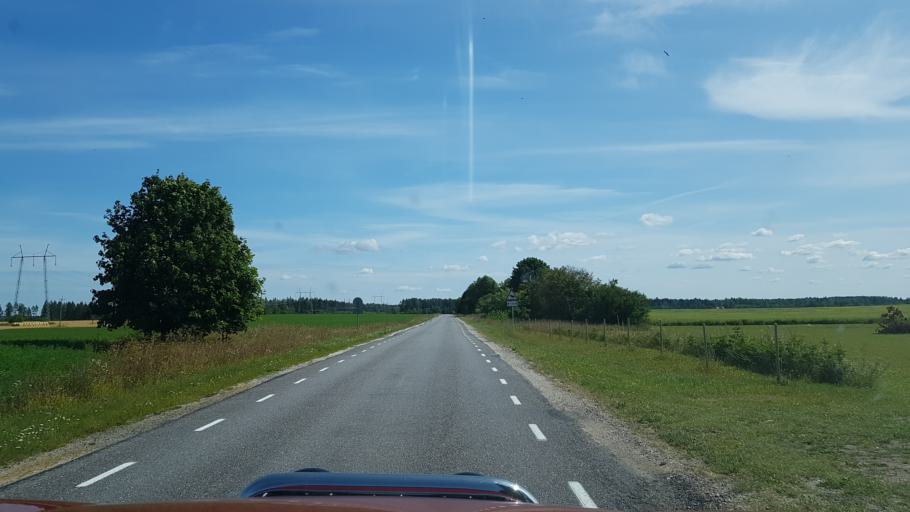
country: EE
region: Laeaene-Virumaa
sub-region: Tapa vald
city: Tapa
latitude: 59.1812
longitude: 25.9554
